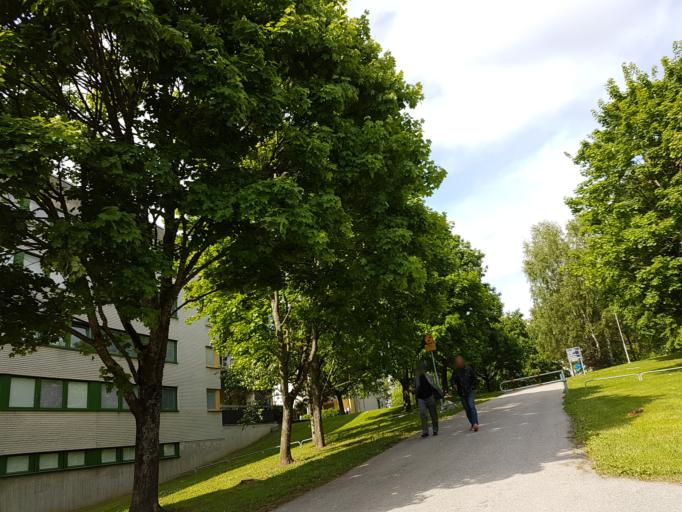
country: SE
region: Stockholm
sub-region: Sundbybergs Kommun
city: Sundbyberg
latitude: 59.3771
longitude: 17.9556
